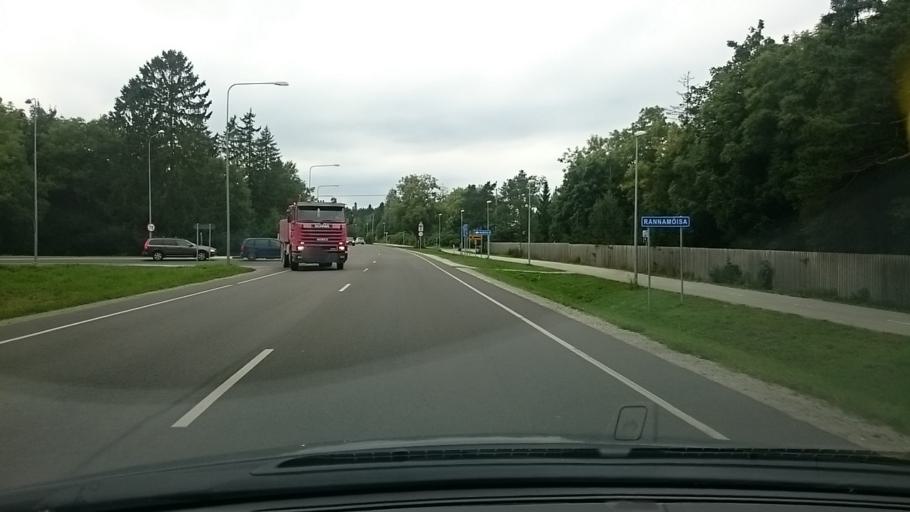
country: EE
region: Harju
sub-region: Harku vald
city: Tabasalu
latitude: 59.4360
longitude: 24.5182
